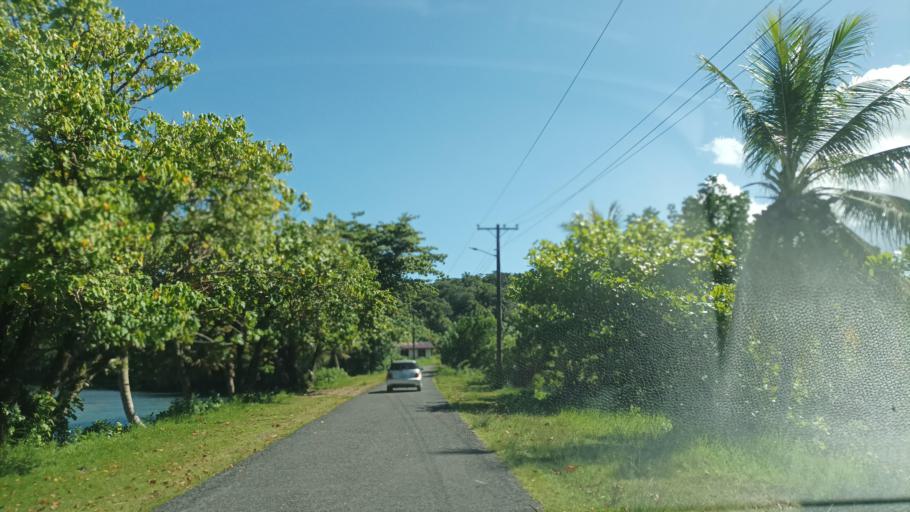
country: FM
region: Pohnpei
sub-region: Madolenihm Municipality
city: Madolenihm Municipality Government
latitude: 6.8443
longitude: 158.3139
